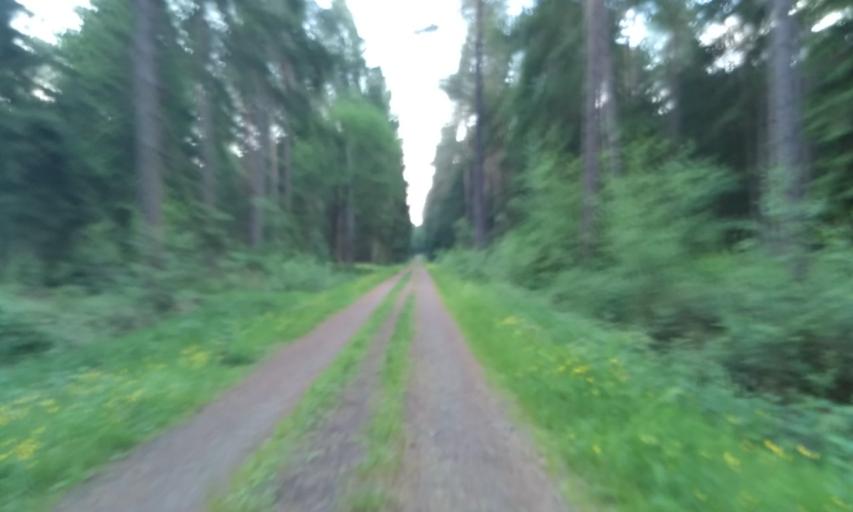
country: DE
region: Lower Saxony
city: Agathenburg
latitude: 53.5264
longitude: 9.5020
